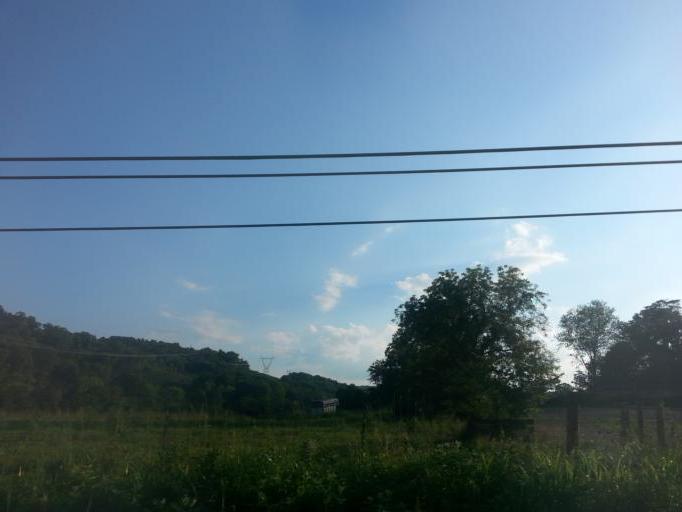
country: US
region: Tennessee
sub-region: Anderson County
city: Clinton
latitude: 36.0401
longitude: -84.1084
